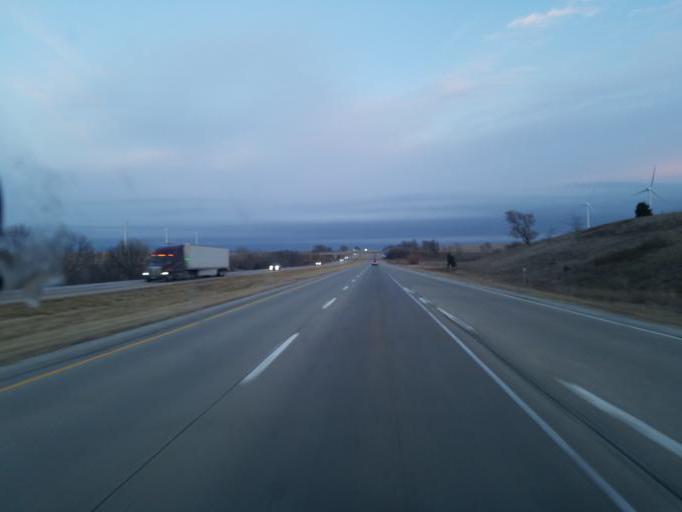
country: US
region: Iowa
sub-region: Pottawattamie County
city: Avoca
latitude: 41.4973
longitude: -95.2565
